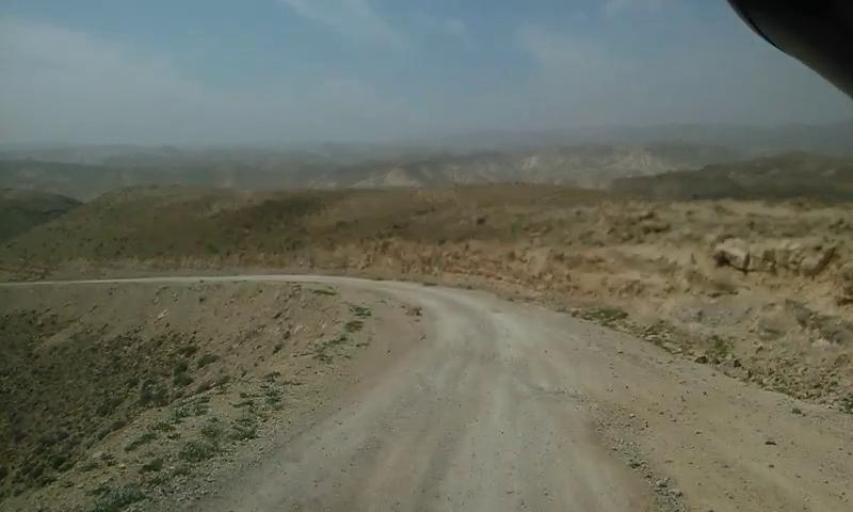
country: PS
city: `Arab ar Rashaydah
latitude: 31.5177
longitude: 35.2947
